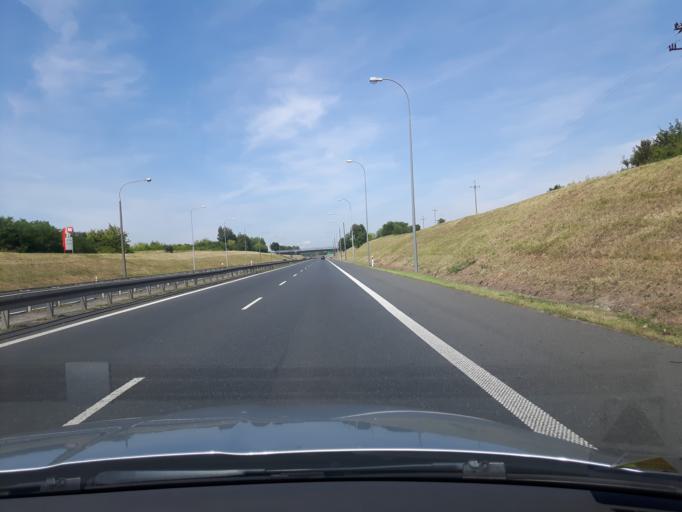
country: PL
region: Masovian Voivodeship
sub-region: Powiat nowodworski
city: Zakroczym
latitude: 52.4307
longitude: 20.6532
